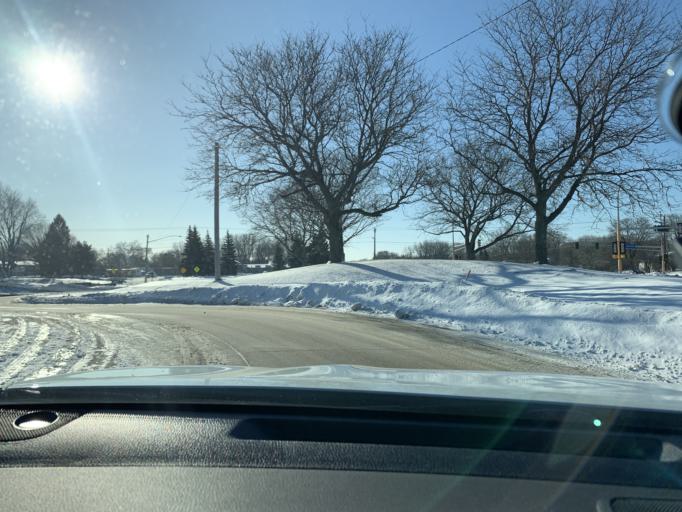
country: US
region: Minnesota
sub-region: Anoka County
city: Fridley
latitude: 45.0943
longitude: -93.2627
